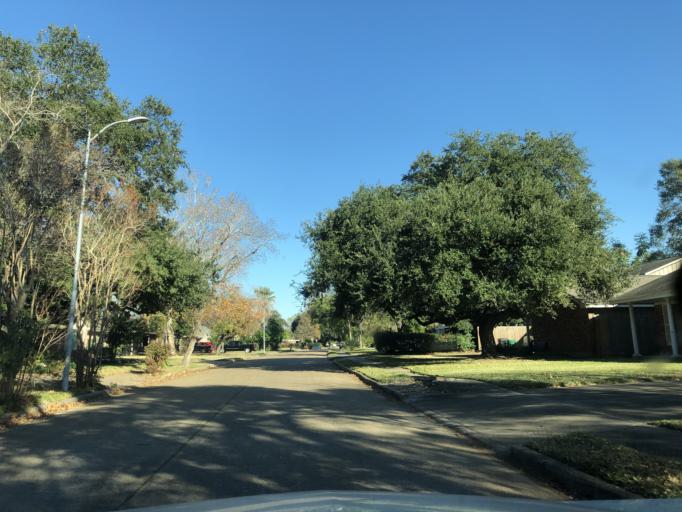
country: US
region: Texas
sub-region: Harris County
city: Bellaire
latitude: 29.6976
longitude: -95.5115
